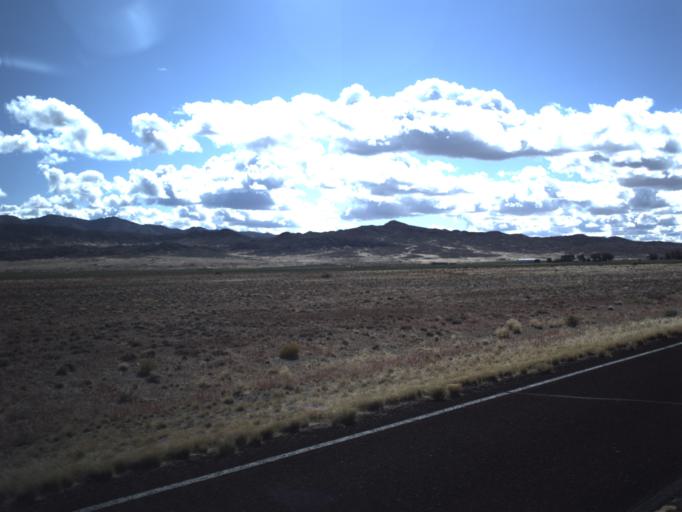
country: US
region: Nevada
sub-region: White Pine County
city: McGill
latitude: 38.9620
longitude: -114.0336
